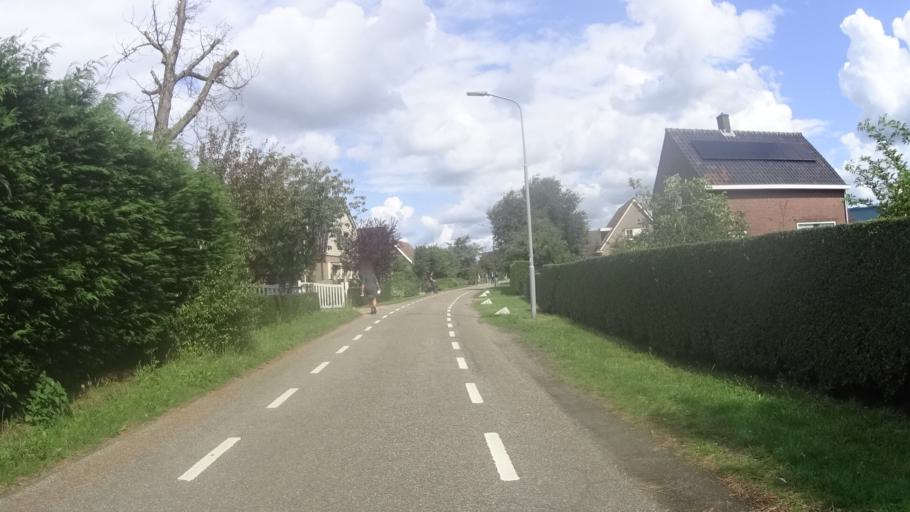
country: NL
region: North Holland
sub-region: Gemeente Beverwijk
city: Beverwijk
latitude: 52.5030
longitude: 4.6503
